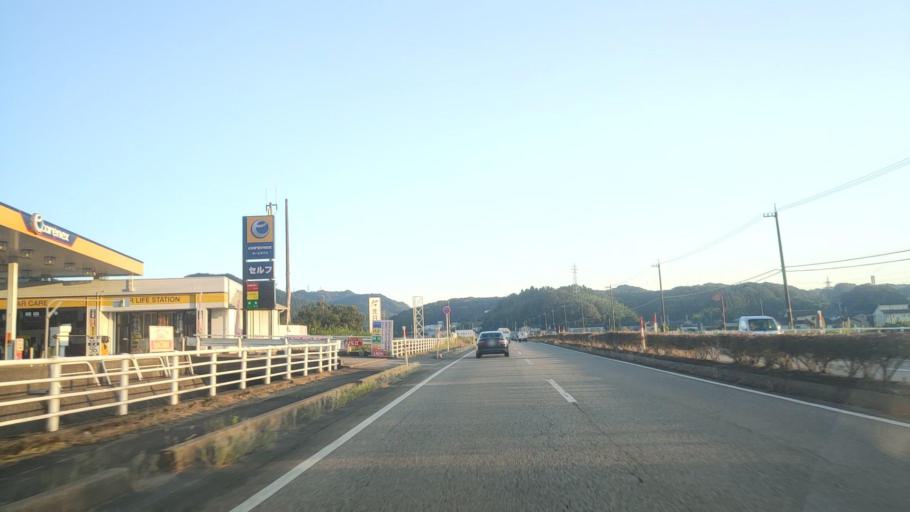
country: JP
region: Toyama
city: Himi
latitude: 36.8147
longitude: 136.9960
